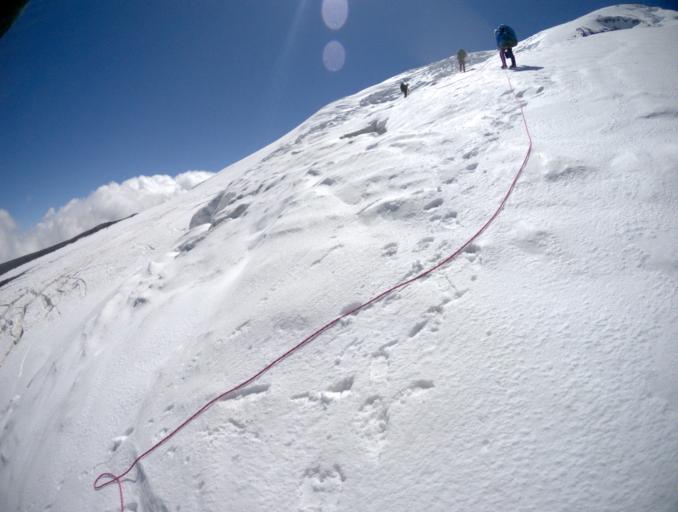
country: RU
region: Kabardino-Balkariya
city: Terskol
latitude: 43.3819
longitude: 42.4447
